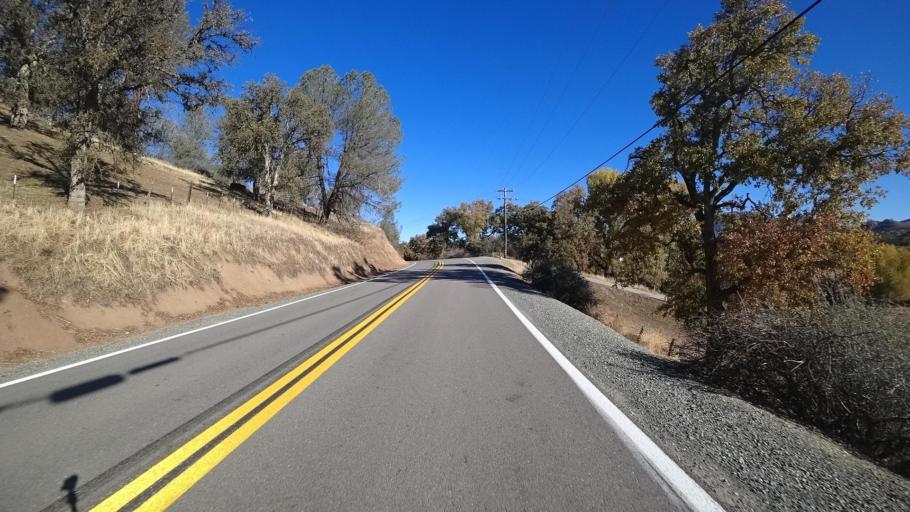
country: US
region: California
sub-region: Kern County
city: Alta Sierra
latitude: 35.7198
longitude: -118.7246
